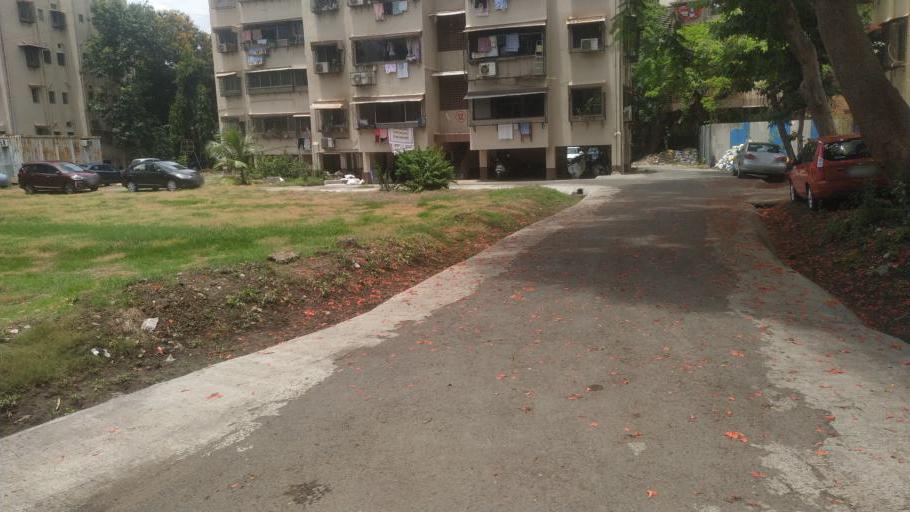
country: IN
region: Maharashtra
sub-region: Mumbai Suburban
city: Mumbai
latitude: 19.0521
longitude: 72.8699
